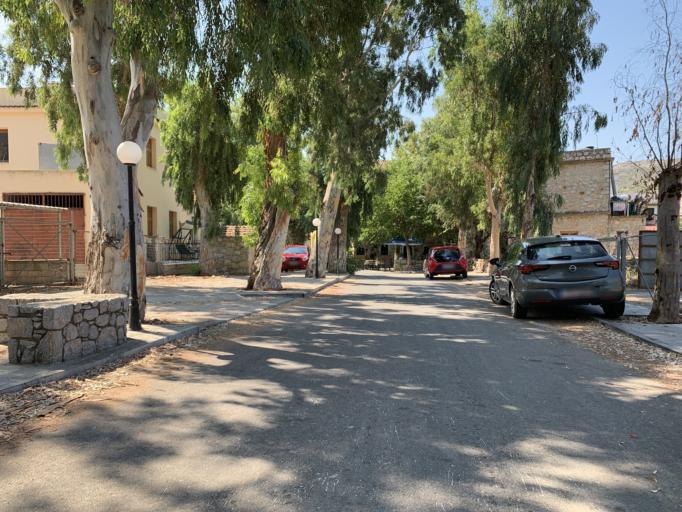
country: GR
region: North Aegean
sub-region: Chios
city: Thymiana
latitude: 38.2977
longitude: 26.0099
